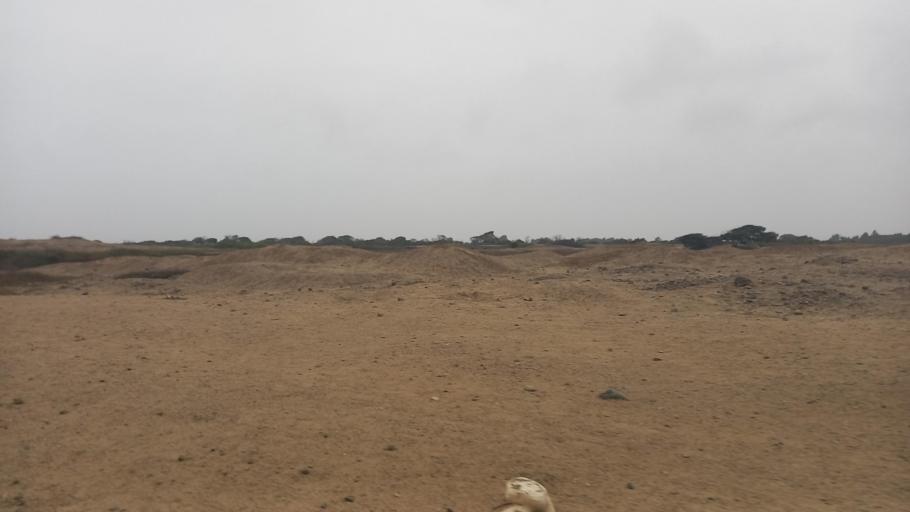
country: PE
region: La Libertad
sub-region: Provincia de Trujillo
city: La Esperanza
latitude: -8.0992
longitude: -79.0780
